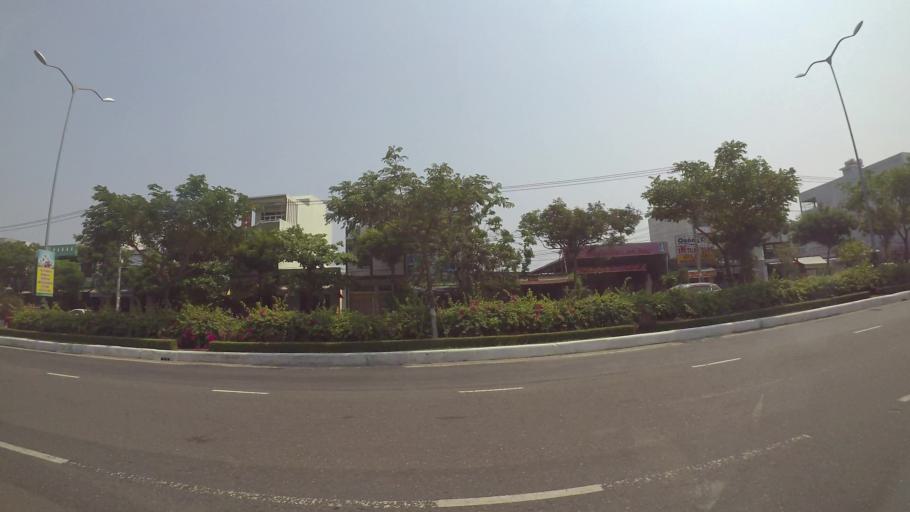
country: VN
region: Da Nang
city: Ngu Hanh Son
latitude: 16.0072
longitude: 108.2586
